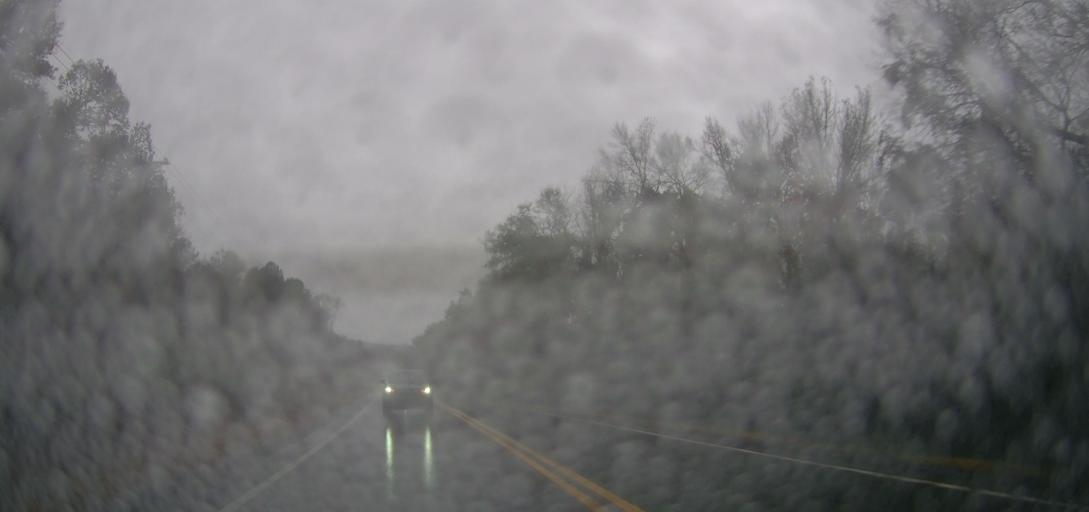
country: US
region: Georgia
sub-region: Putnam County
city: Eatonton
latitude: 33.2336
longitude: -83.4353
